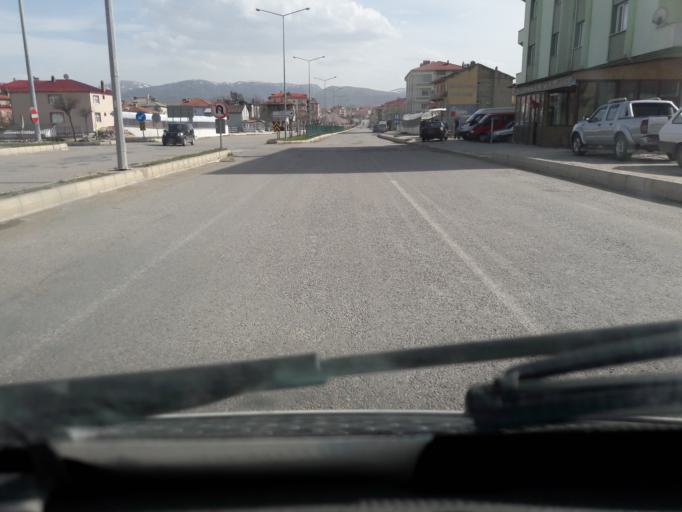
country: TR
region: Gumushane
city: Kelkit
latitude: 40.1360
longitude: 39.4332
